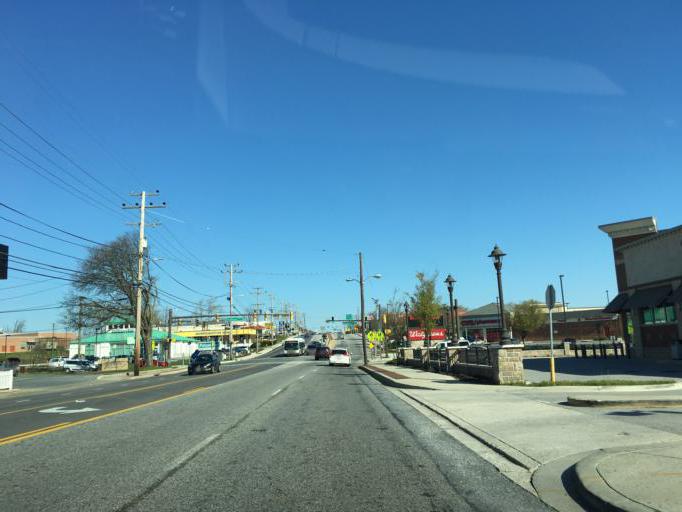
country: US
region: Maryland
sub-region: Baltimore County
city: Towson
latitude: 39.4090
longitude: -76.6083
